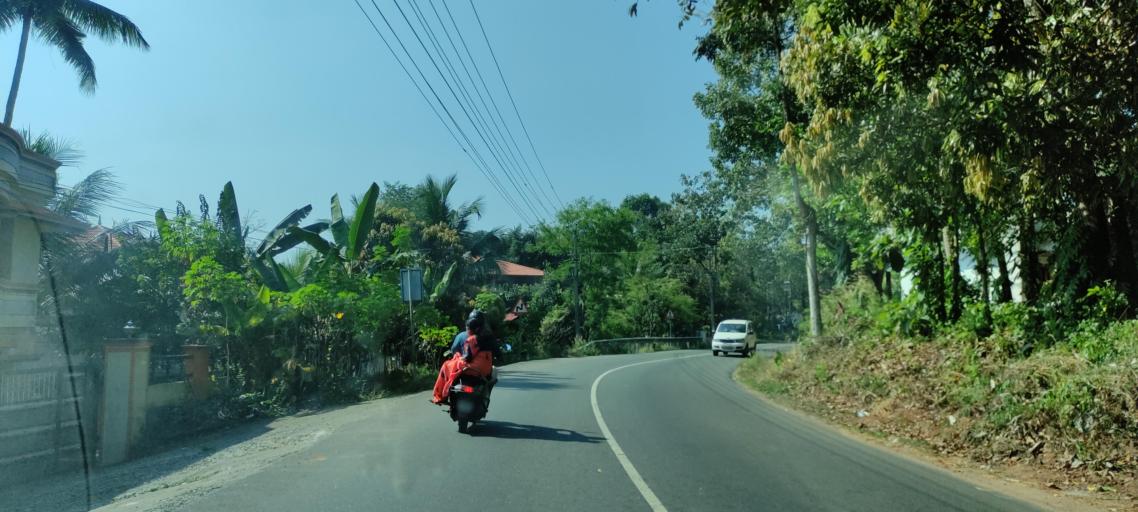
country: IN
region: Kerala
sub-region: Pattanamtitta
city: Adur
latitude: 9.1036
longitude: 76.6905
